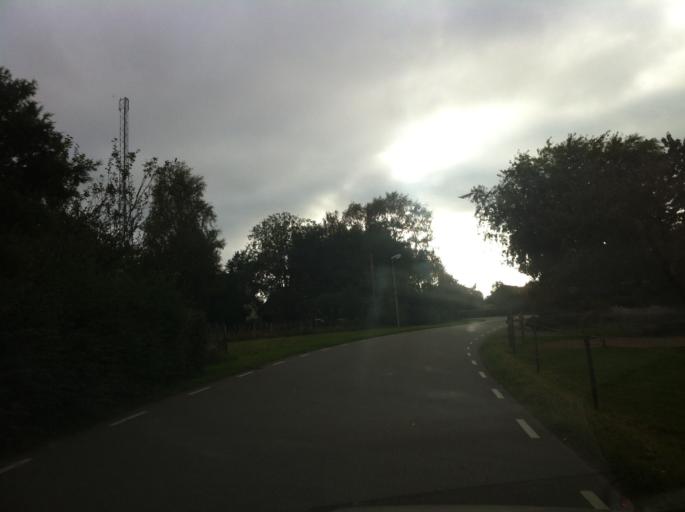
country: SE
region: Skane
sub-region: Helsingborg
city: Morarp
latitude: 56.0372
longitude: 12.8381
